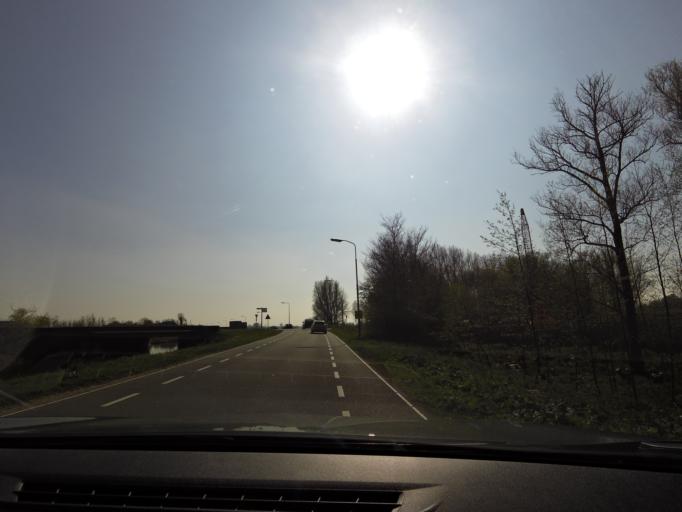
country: NL
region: South Holland
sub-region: Gemeente Westland
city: De Lier
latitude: 51.9501
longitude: 4.2781
